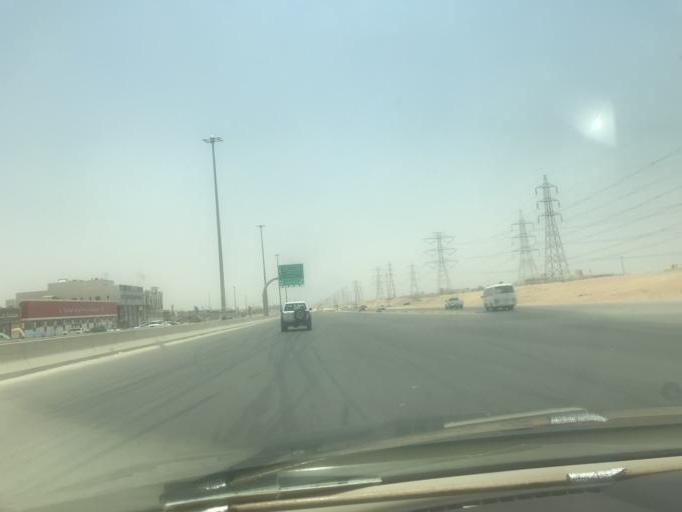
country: SA
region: Ar Riyad
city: Riyadh
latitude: 24.8227
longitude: 46.7465
